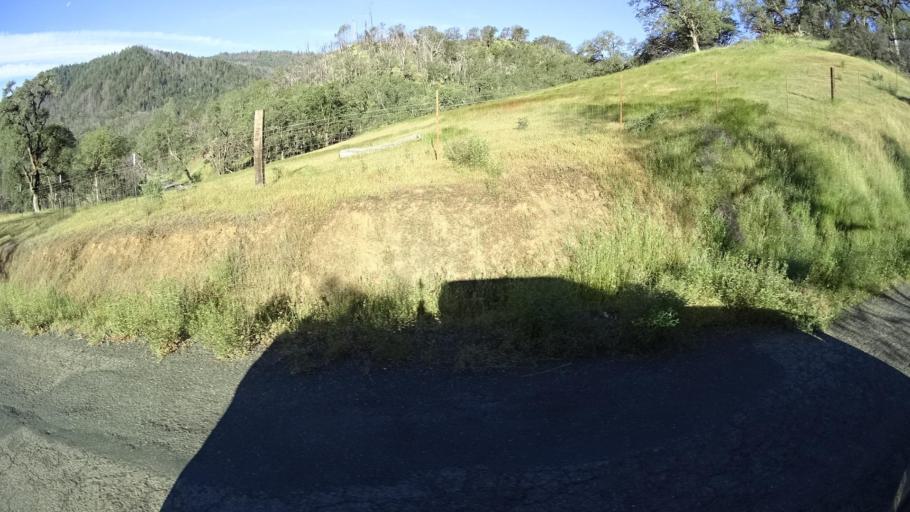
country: US
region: California
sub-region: Lake County
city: Upper Lake
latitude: 39.2567
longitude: -122.9473
